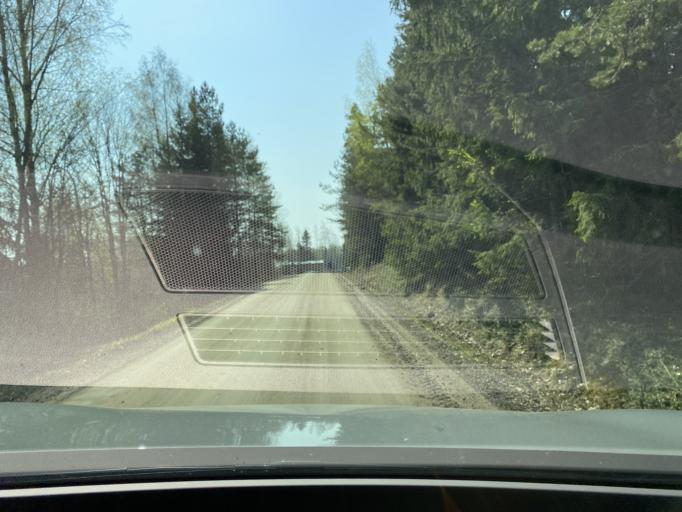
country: FI
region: Satakunta
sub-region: Pori
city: Huittinen
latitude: 61.1278
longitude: 22.8345
